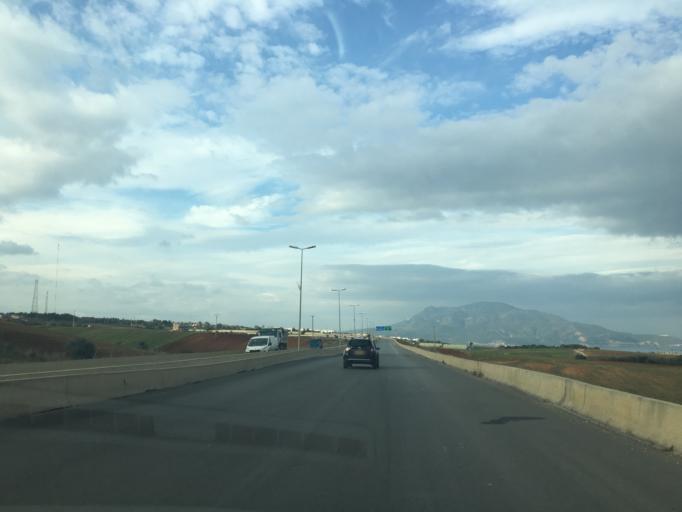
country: DZ
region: Tipaza
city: Tipasa
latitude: 36.5766
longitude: 2.5091
